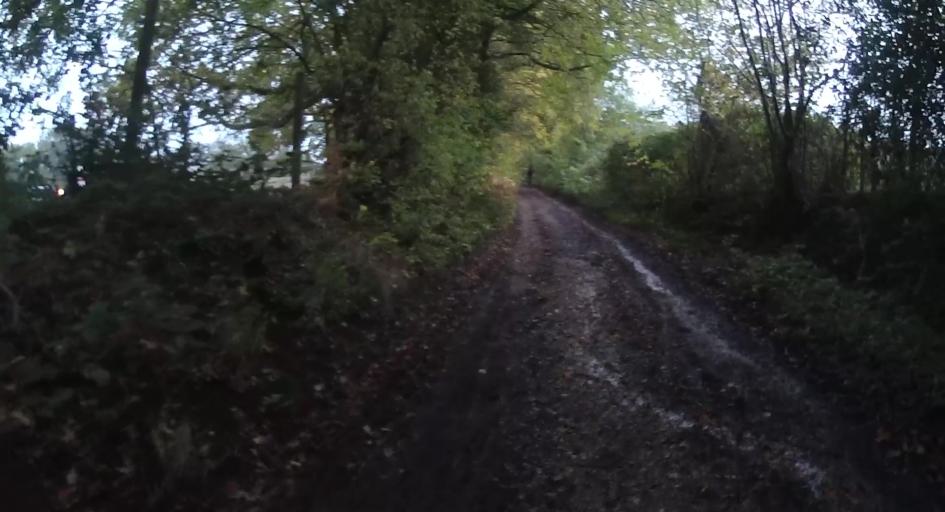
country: GB
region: England
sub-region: Surrey
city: Farnham
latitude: 51.2285
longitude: -0.8107
